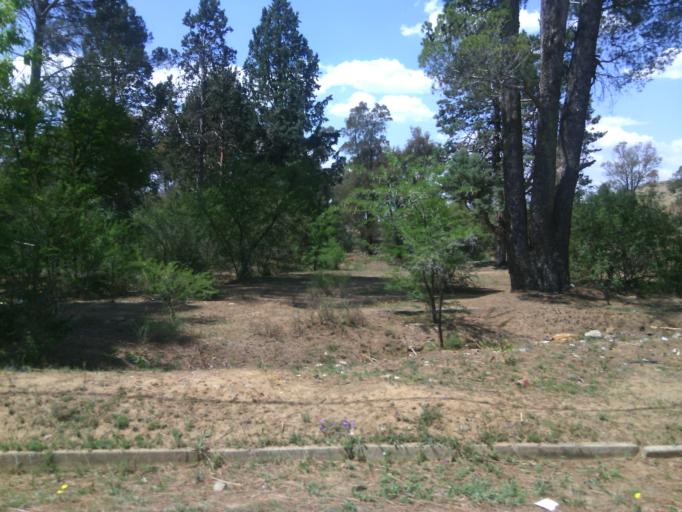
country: ZA
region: Orange Free State
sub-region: Xhariep District Municipality
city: Dewetsdorp
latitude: -29.5869
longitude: 26.6660
